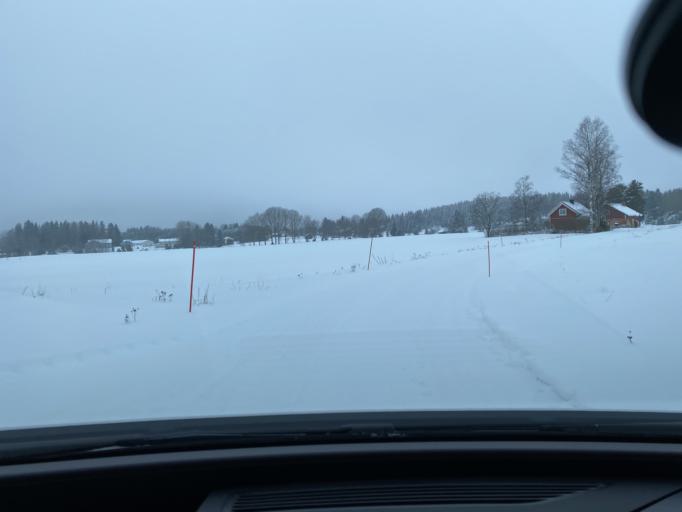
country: FI
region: Pirkanmaa
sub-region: Lounais-Pirkanmaa
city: Punkalaidun
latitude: 61.1271
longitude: 23.0877
